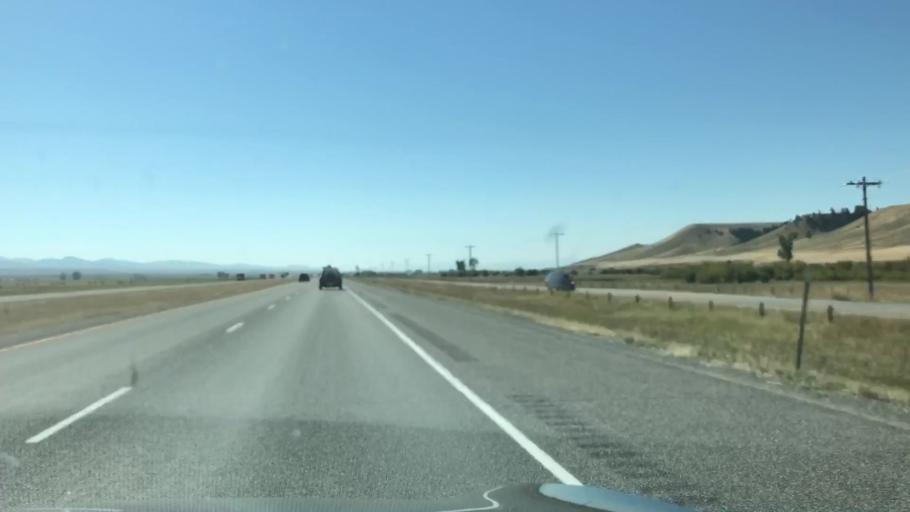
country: US
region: Montana
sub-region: Powell County
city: Deer Lodge
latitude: 46.4734
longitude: -112.7233
